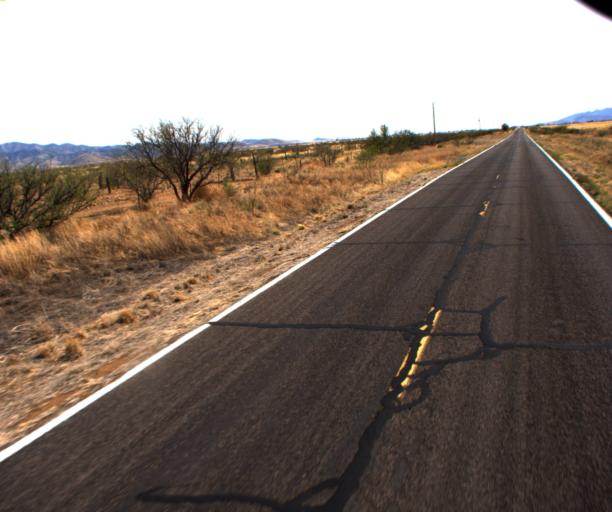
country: US
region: Arizona
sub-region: Cochise County
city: Willcox
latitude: 31.9163
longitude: -109.4915
